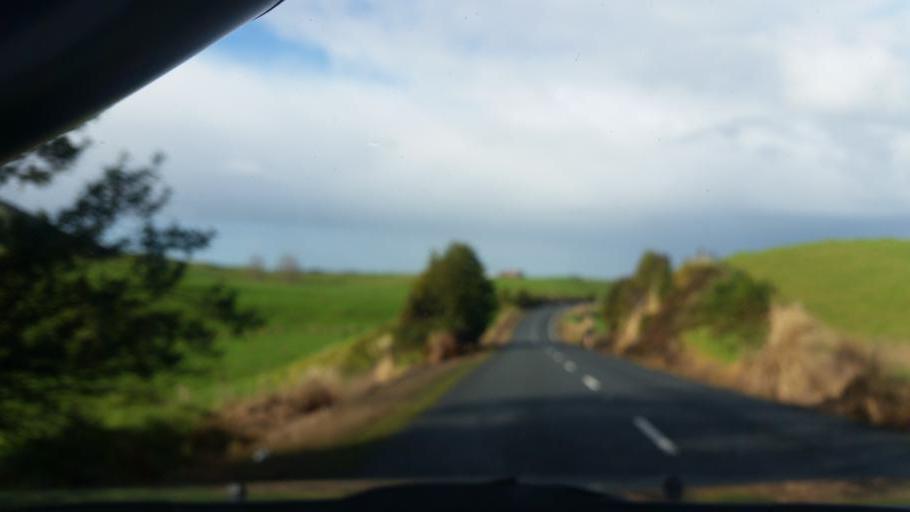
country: NZ
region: Northland
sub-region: Kaipara District
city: Dargaville
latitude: -35.8141
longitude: 173.9250
